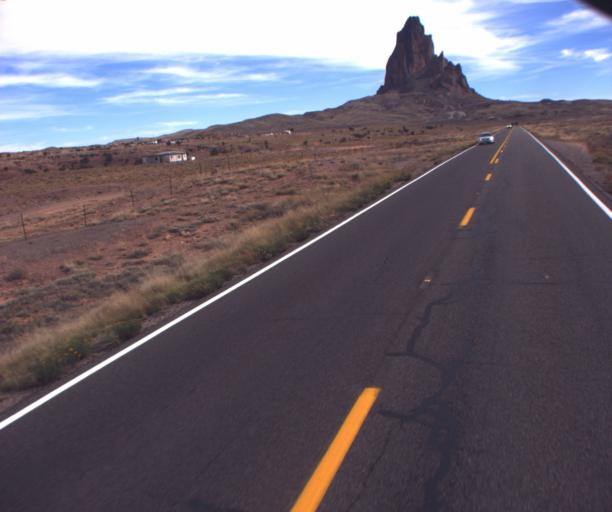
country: US
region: Arizona
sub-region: Navajo County
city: Kayenta
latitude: 36.8359
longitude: -110.2520
